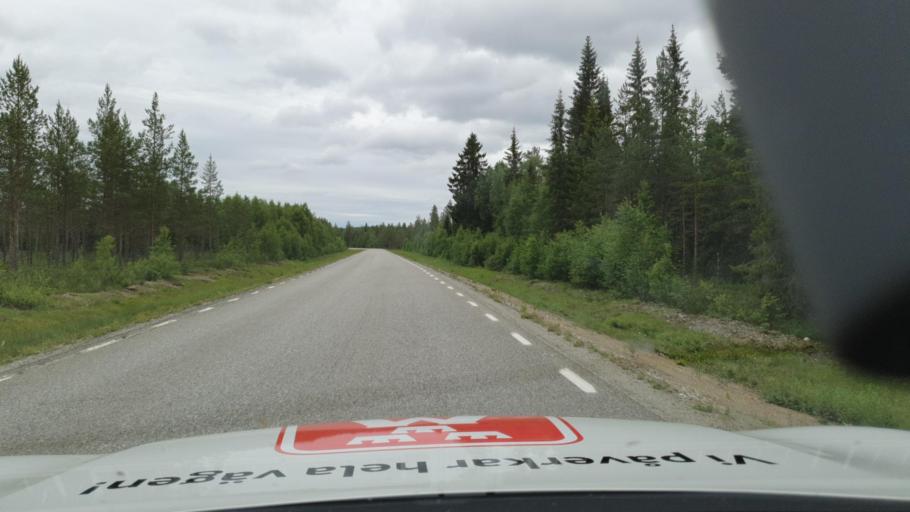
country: SE
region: Vaesterbotten
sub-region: Lycksele Kommun
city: Lycksele
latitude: 64.1862
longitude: 18.3144
